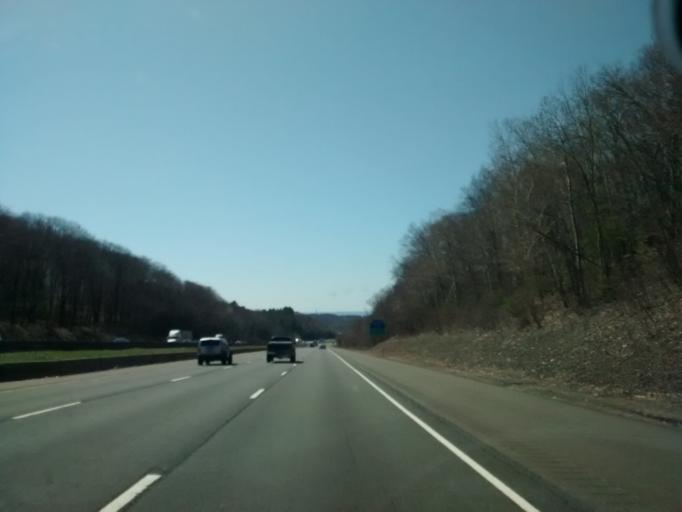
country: US
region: Connecticut
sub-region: Tolland County
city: Rockville
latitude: 41.8545
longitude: -72.4089
